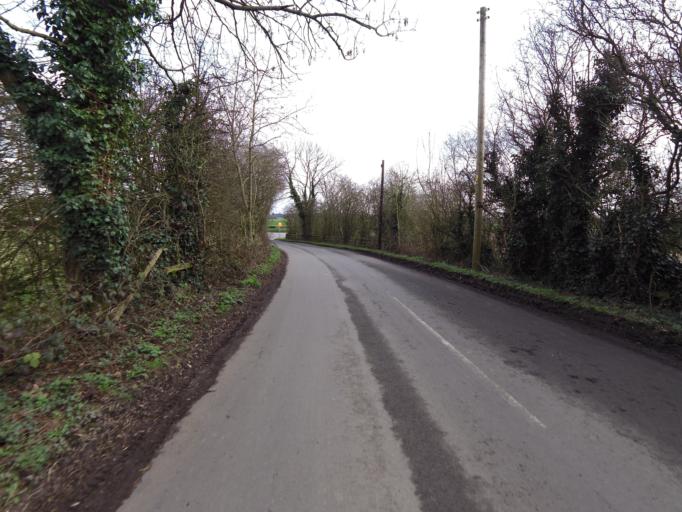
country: GB
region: England
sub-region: Doncaster
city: Moss
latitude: 53.5922
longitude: -1.0929
